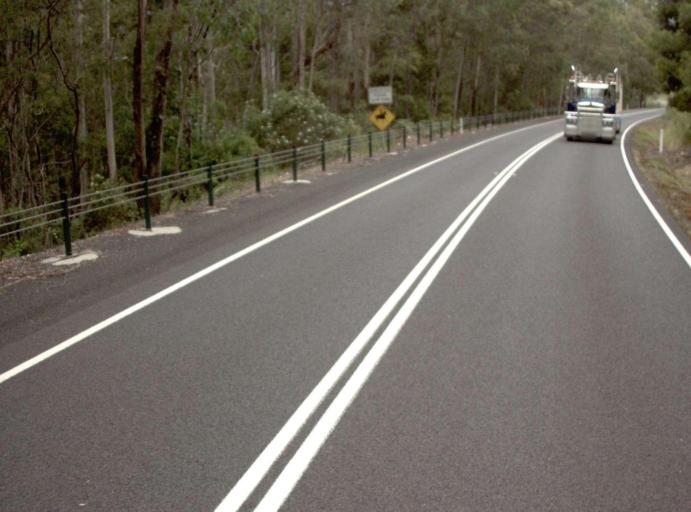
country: AU
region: New South Wales
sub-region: Bombala
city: Bombala
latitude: -37.3287
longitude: 149.2066
